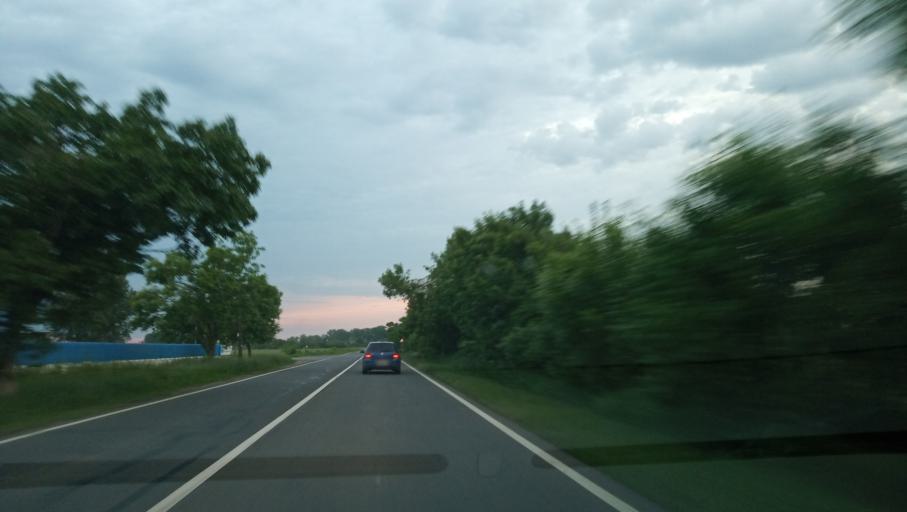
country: RO
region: Timis
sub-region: Comuna Sag
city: Sag
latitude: 45.6306
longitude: 21.1887
